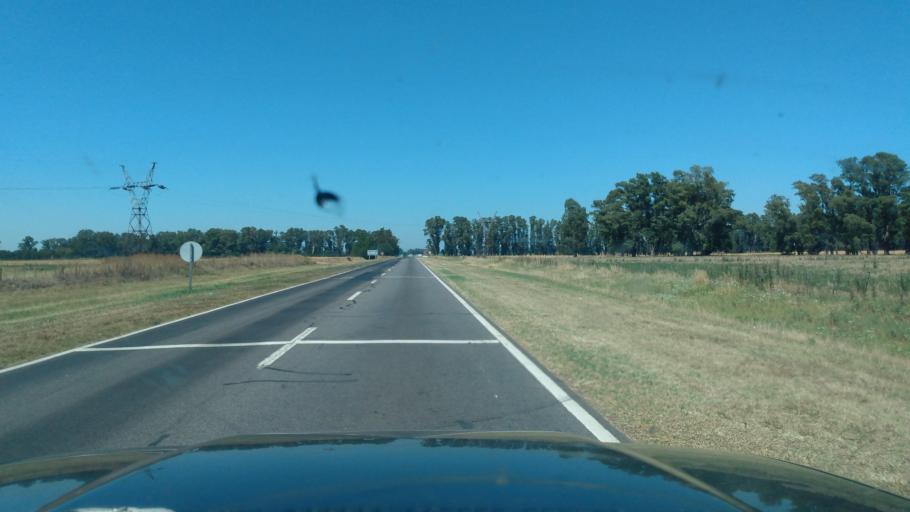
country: AR
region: Buenos Aires
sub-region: Partido de Bragado
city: Bragado
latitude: -35.0931
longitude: -60.3955
